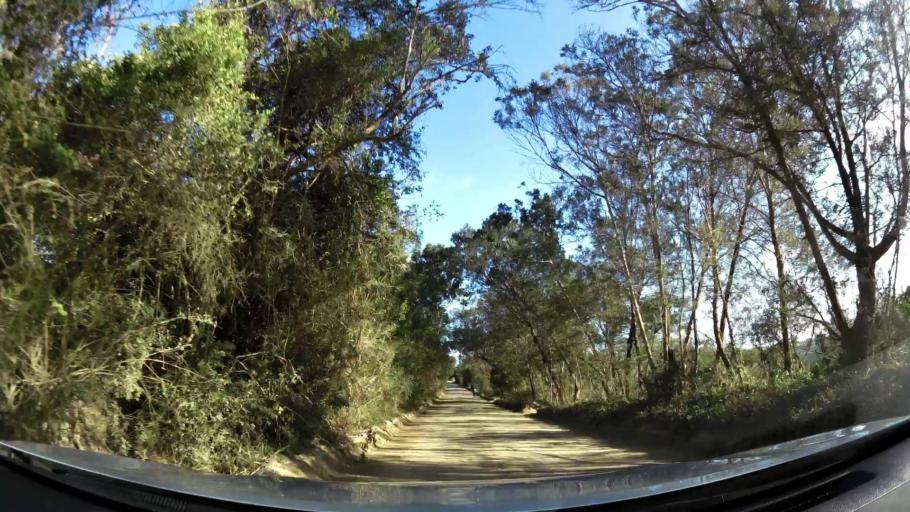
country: ZA
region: Western Cape
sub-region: Eden District Municipality
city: George
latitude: -33.9863
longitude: 22.5680
